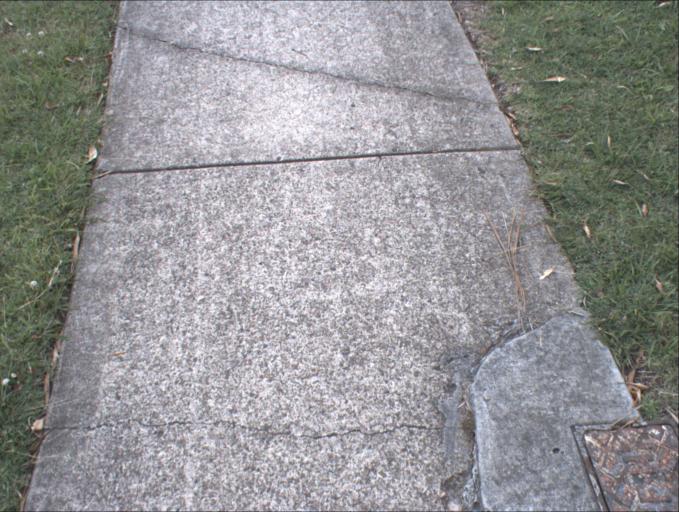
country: AU
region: Queensland
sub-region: Logan
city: Woodridge
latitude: -27.6157
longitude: 153.1093
